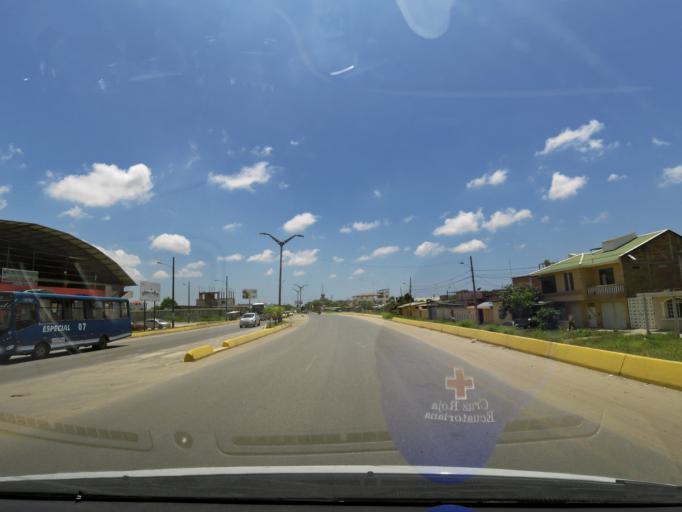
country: EC
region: El Oro
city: Huaquillas
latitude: -3.4838
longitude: -80.2165
